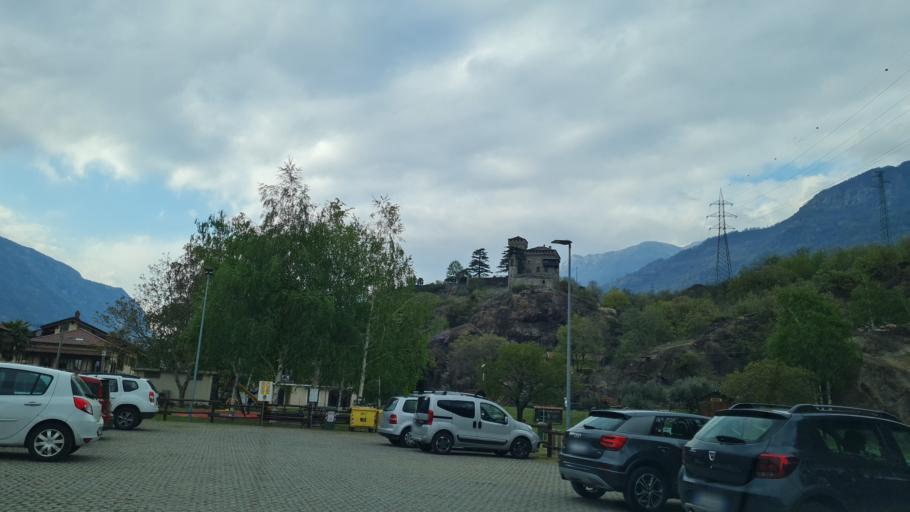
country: IT
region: Piedmont
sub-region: Provincia di Torino
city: Settimo Vittone
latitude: 45.5376
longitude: 7.8394
